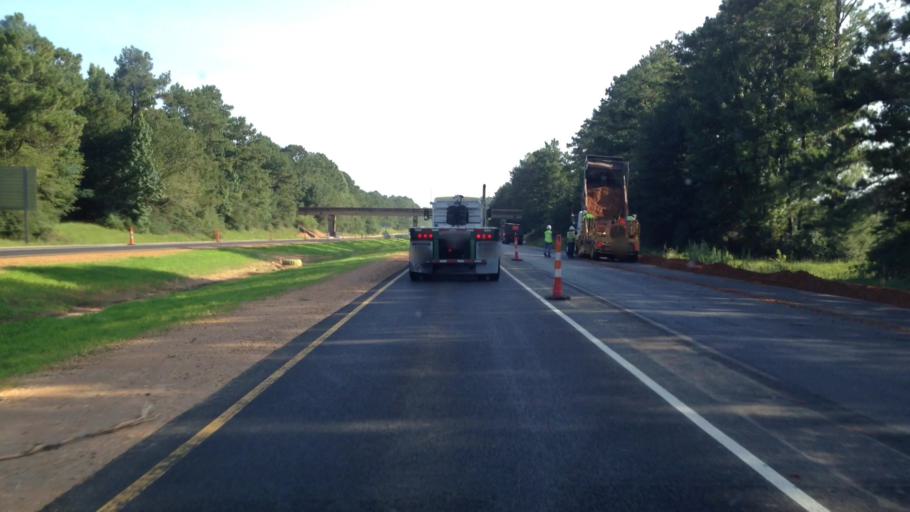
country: US
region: Mississippi
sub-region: Pike County
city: McComb
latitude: 31.2028
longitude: -90.4839
